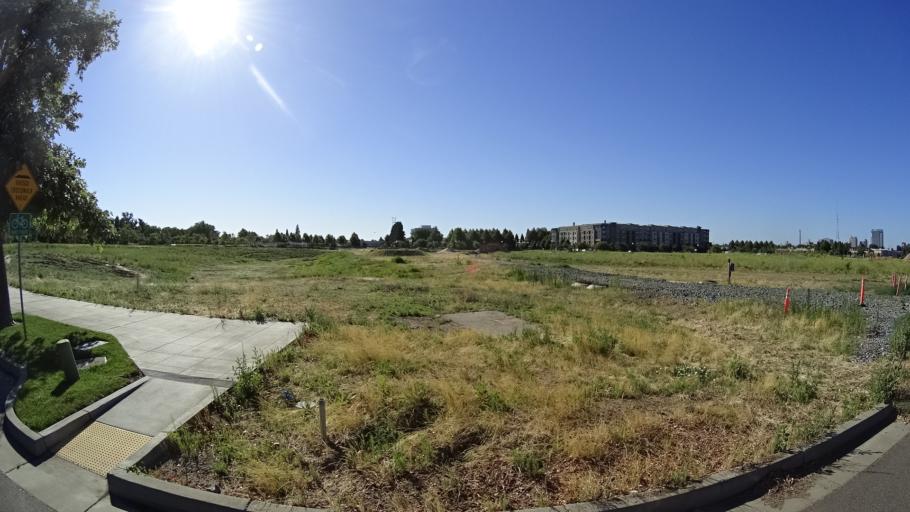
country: US
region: California
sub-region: Sacramento County
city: Sacramento
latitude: 38.6008
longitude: -121.4931
